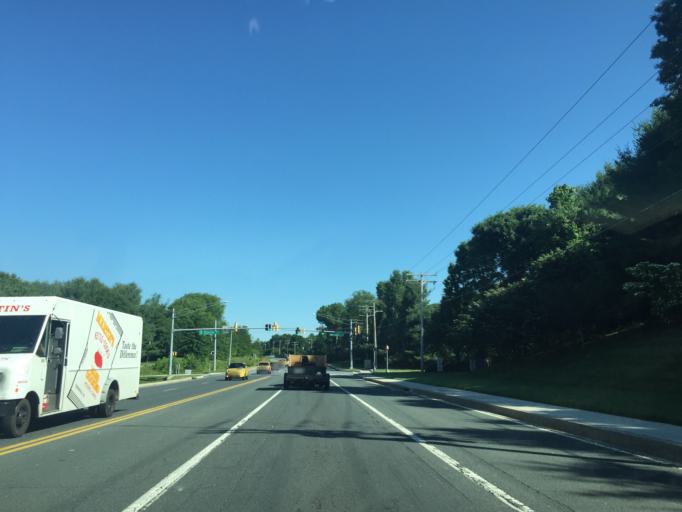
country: US
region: Maryland
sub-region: Harford County
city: Bel Air North
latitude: 39.5644
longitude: -76.3741
